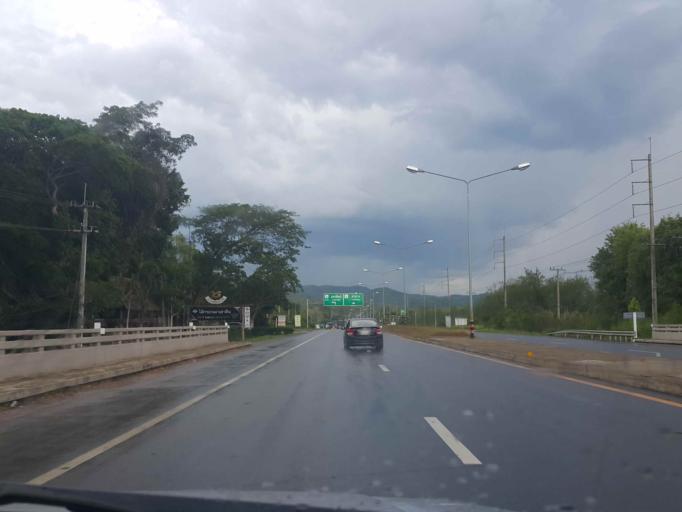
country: TH
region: Phrae
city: Den Chai
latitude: 17.9719
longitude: 100.0736
